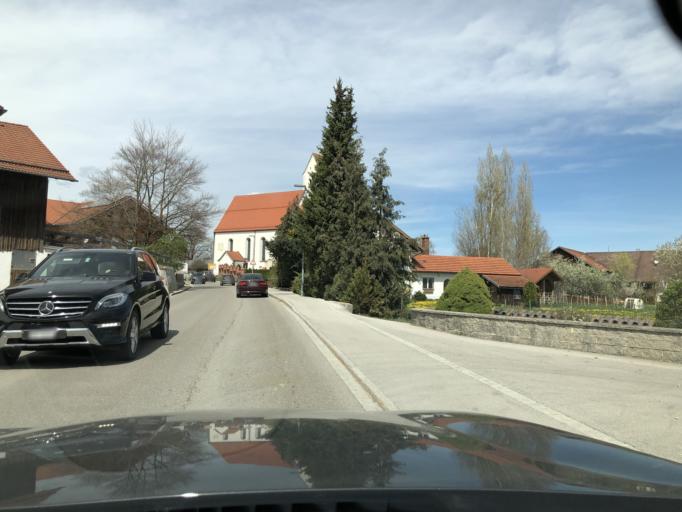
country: DE
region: Bavaria
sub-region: Swabia
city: Lengenwang
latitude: 47.6977
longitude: 10.6045
